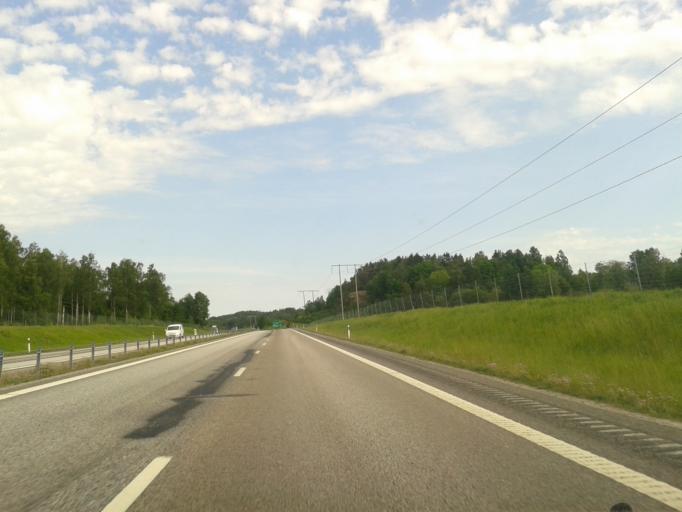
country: SE
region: Vaestra Goetaland
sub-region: Munkedals Kommun
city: Munkedal
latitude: 58.5231
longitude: 11.5470
